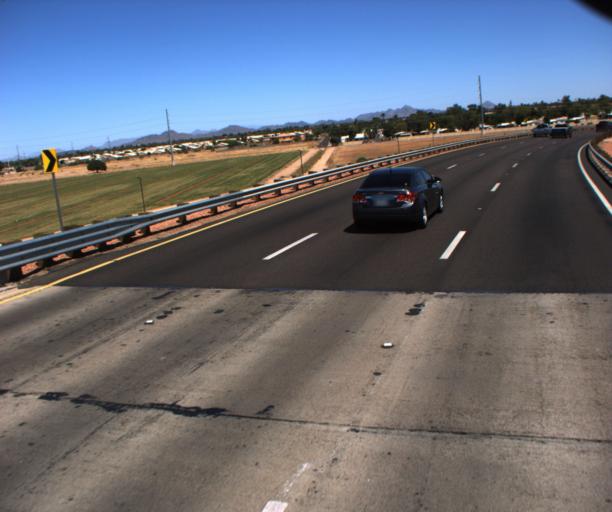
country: US
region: Arizona
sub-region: Maricopa County
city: Peoria
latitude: 33.5633
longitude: -112.2153
